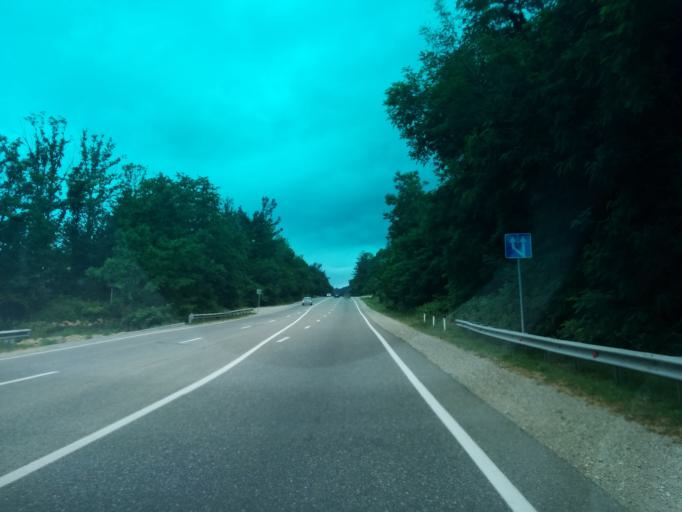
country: RU
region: Krasnodarskiy
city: Ol'ginka
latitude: 44.1788
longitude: 38.9398
